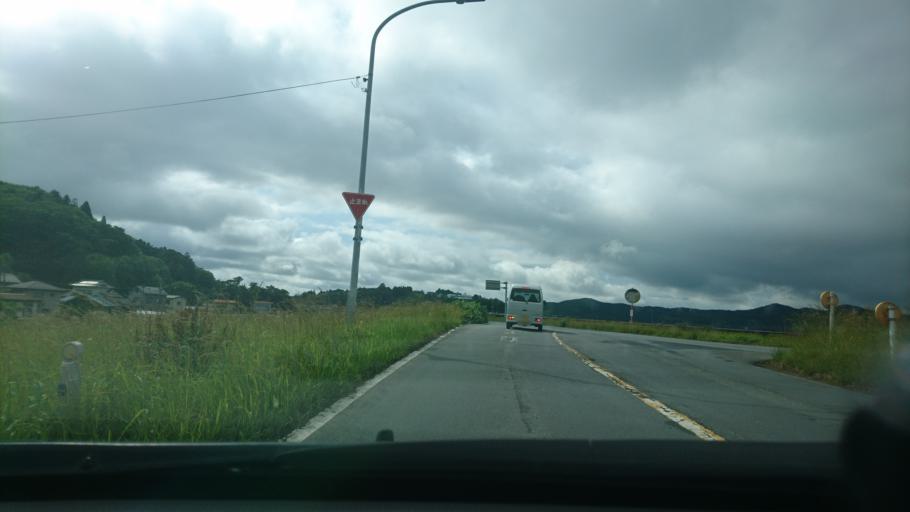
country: JP
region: Miyagi
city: Ishinomaki
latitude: 38.5099
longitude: 141.3097
